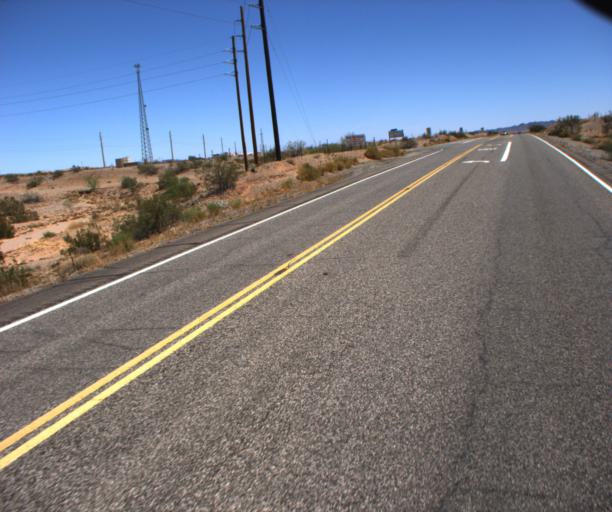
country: US
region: Arizona
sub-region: La Paz County
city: Parker
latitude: 34.0031
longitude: -114.2338
